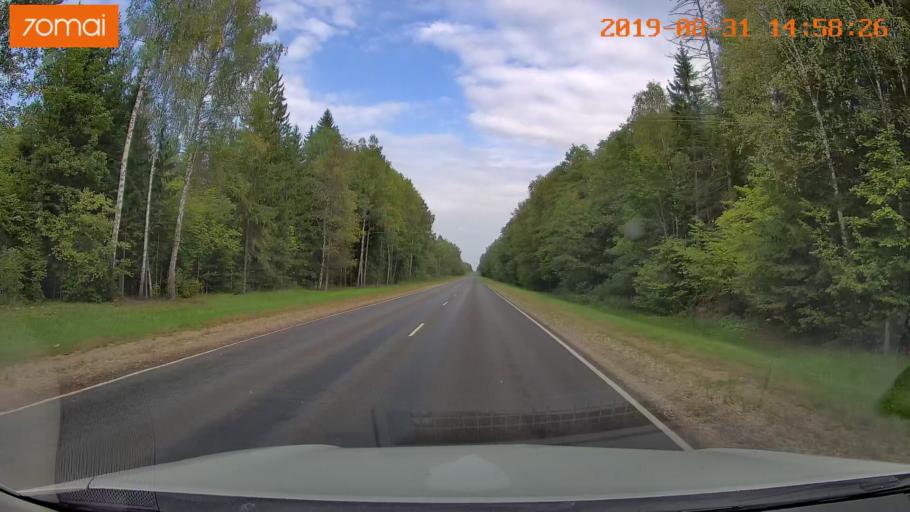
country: RU
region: Kaluga
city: Spas-Demensk
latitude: 54.3176
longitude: 33.9818
